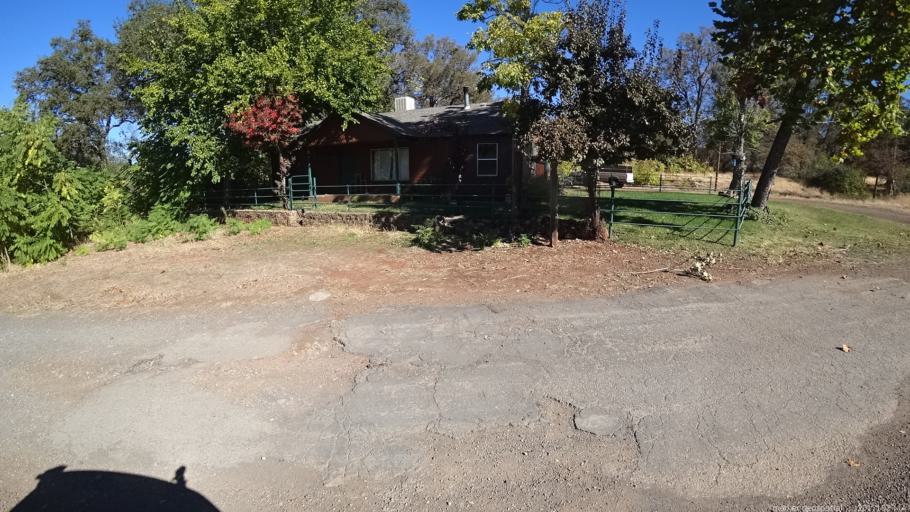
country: US
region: California
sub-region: Shasta County
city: Bella Vista
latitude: 40.6938
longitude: -122.0320
